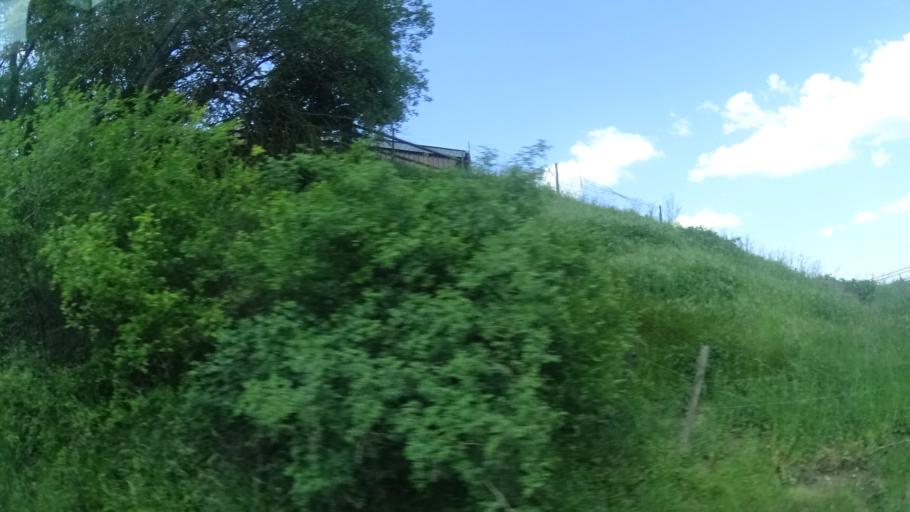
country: DE
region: Thuringia
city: Empfertshausen
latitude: 50.6681
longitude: 10.1014
